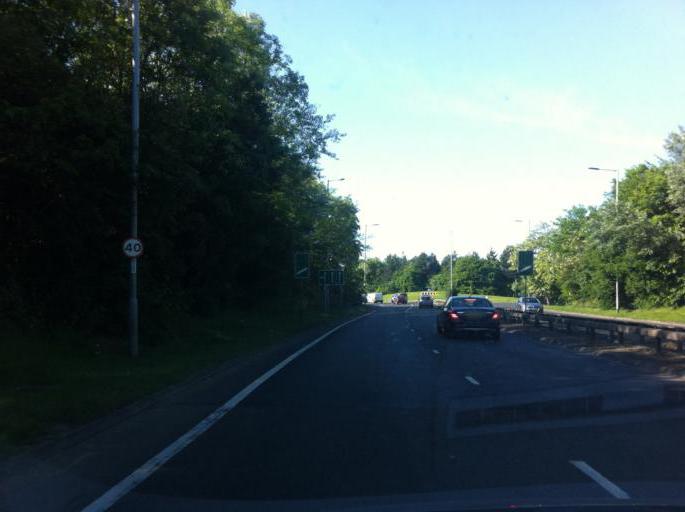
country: GB
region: England
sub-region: Greater London
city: Southall
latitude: 51.5271
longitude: -0.3901
